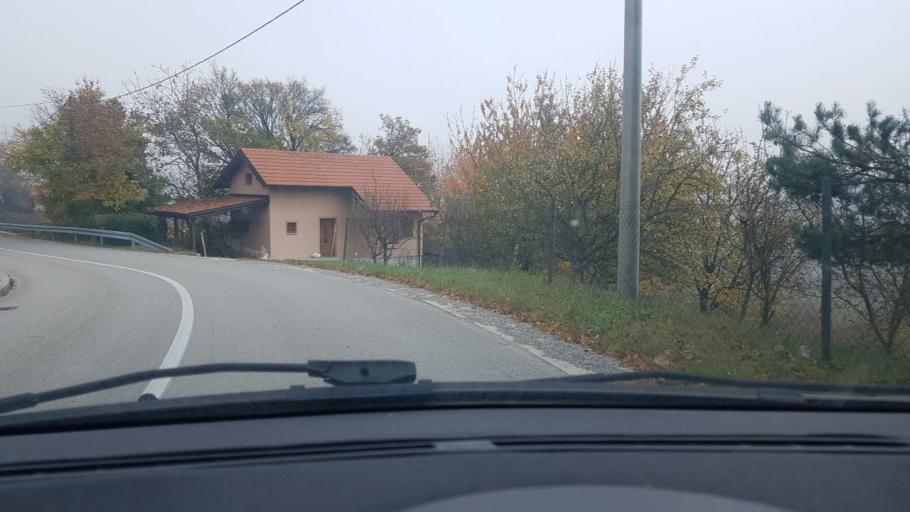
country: HR
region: Varazdinska
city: Ivanec
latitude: 46.1406
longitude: 16.1513
